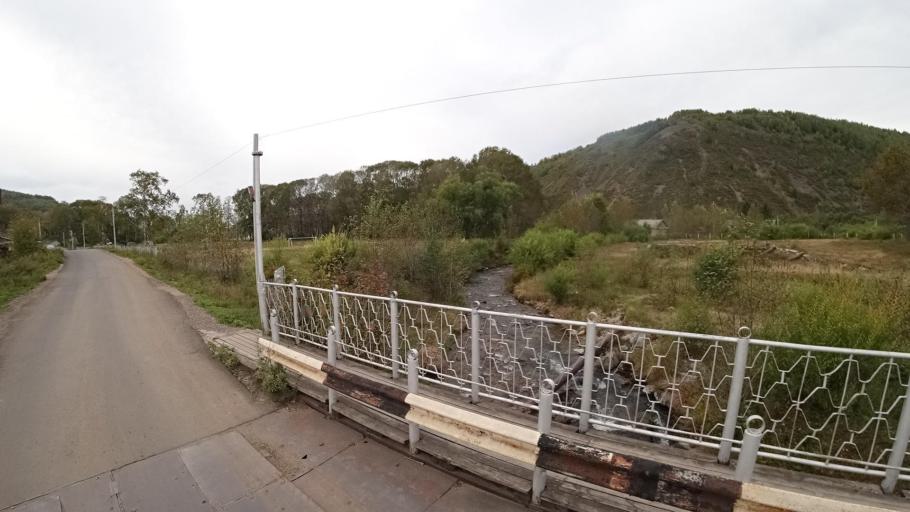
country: RU
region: Jewish Autonomous Oblast
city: Khingansk
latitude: 49.1286
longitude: 131.1978
